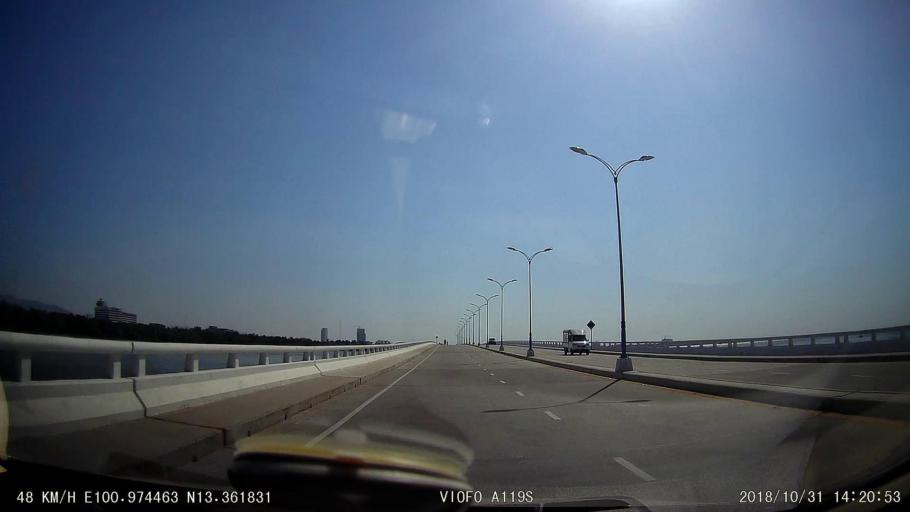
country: TH
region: Chon Buri
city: Chon Buri
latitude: 13.3621
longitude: 100.9744
